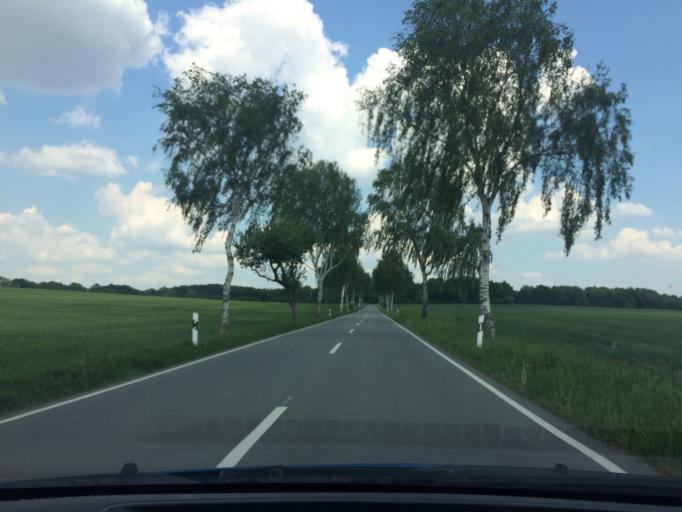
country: DE
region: Lower Saxony
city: Nahrendorf
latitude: 53.1948
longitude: 10.7862
